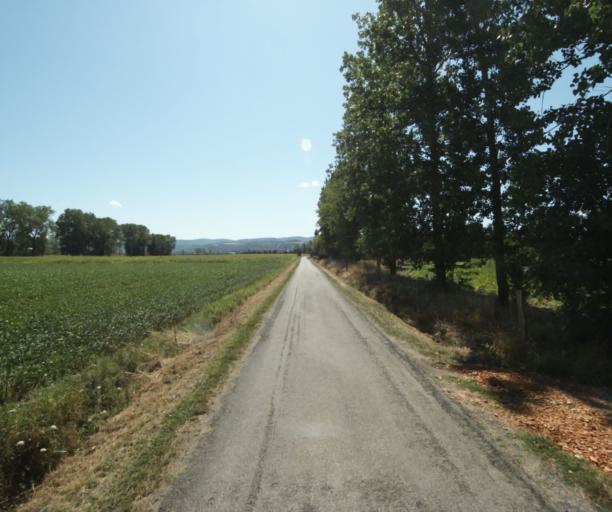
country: FR
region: Midi-Pyrenees
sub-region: Departement de la Haute-Garonne
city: Revel
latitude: 43.4645
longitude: 1.9658
